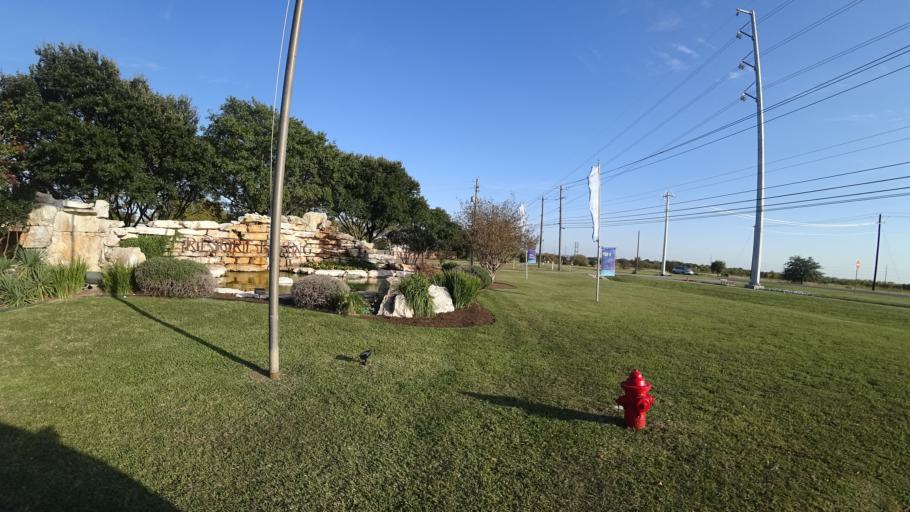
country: US
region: Texas
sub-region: Travis County
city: Pflugerville
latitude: 30.4138
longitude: -97.6527
